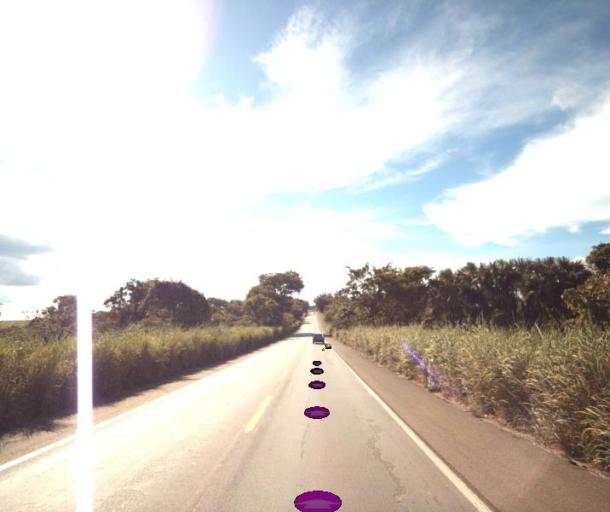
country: BR
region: Goias
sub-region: Uruana
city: Uruana
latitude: -15.5167
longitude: -49.4703
